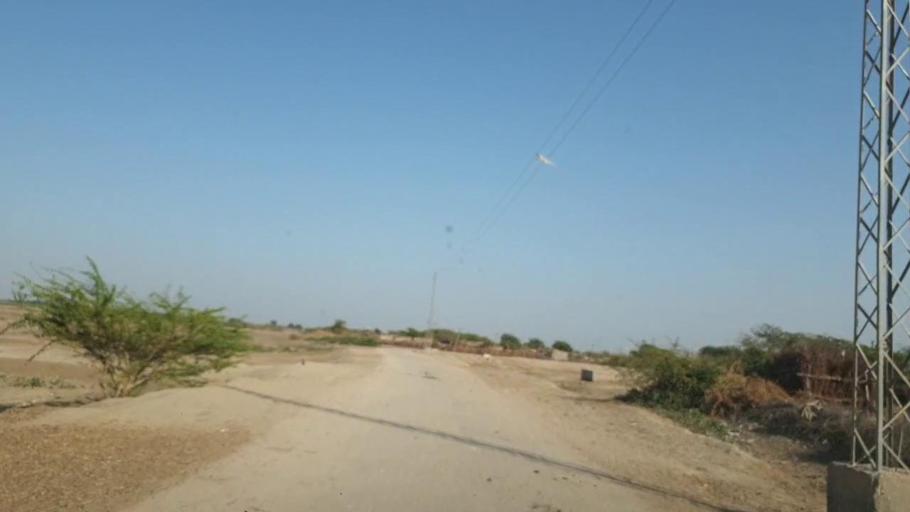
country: PK
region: Sindh
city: Naukot
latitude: 25.0300
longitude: 69.4494
